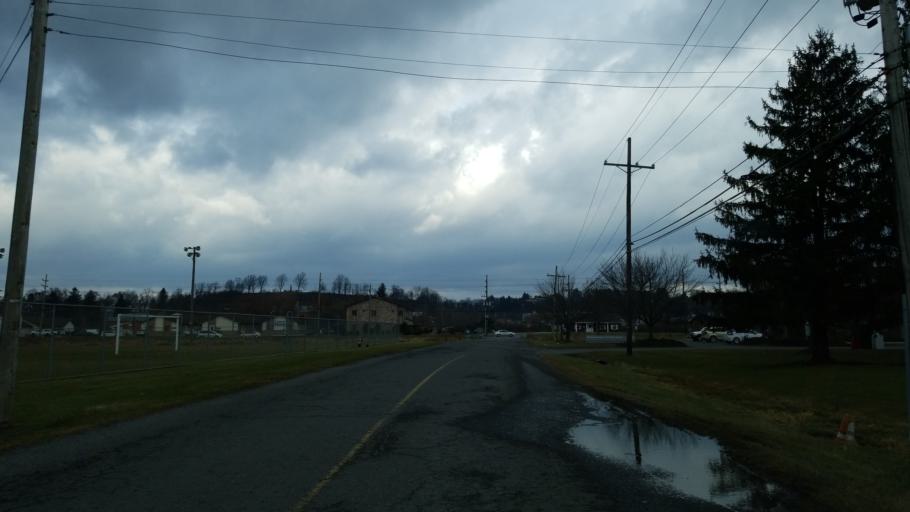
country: US
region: Pennsylvania
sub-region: Clearfield County
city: DuBois
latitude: 41.1221
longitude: -78.7527
